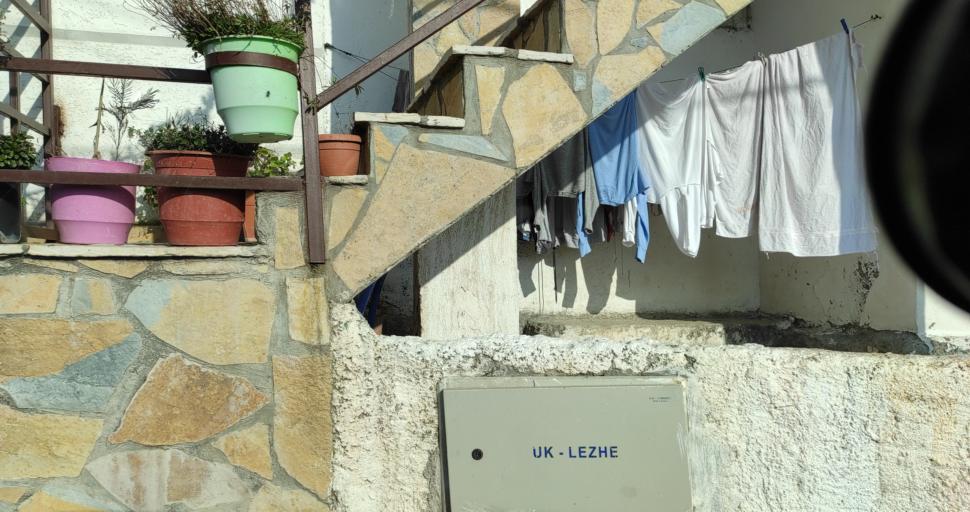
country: AL
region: Lezhe
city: Lezhe
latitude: 41.7889
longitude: 19.6461
